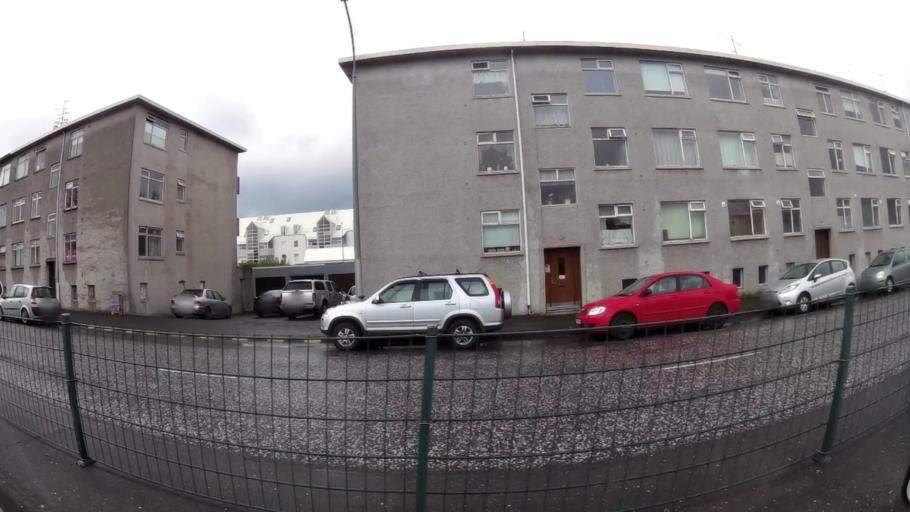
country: IS
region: Capital Region
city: Seltjarnarnes
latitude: 64.1488
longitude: -21.9598
